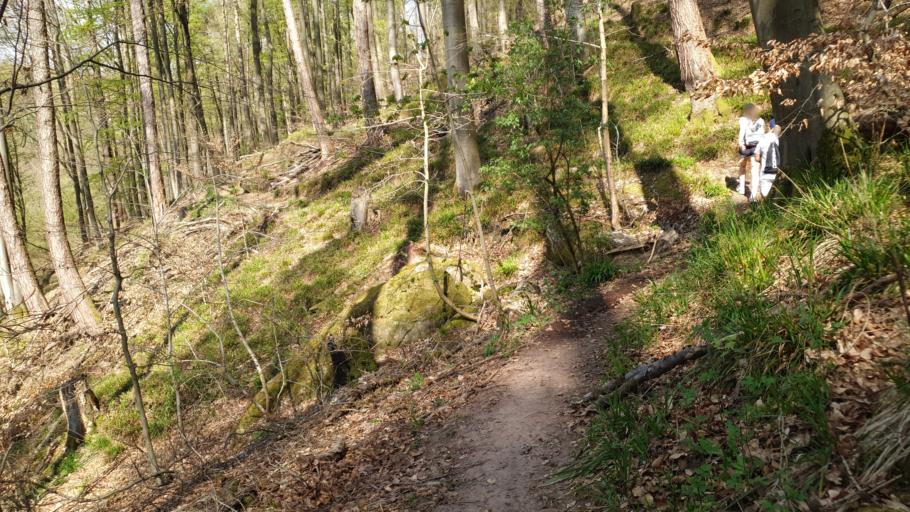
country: DE
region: Rheinland-Pfalz
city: Pirmasens
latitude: 49.2227
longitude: 7.6176
